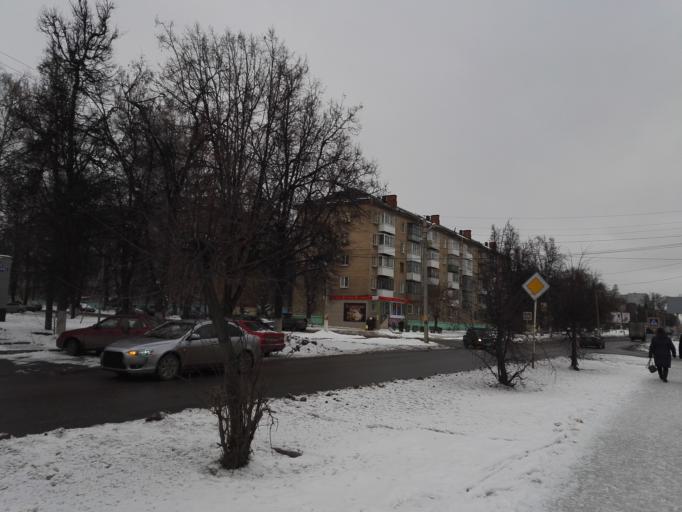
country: RU
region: Tula
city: Novomoskovsk
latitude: 54.0107
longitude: 38.3047
